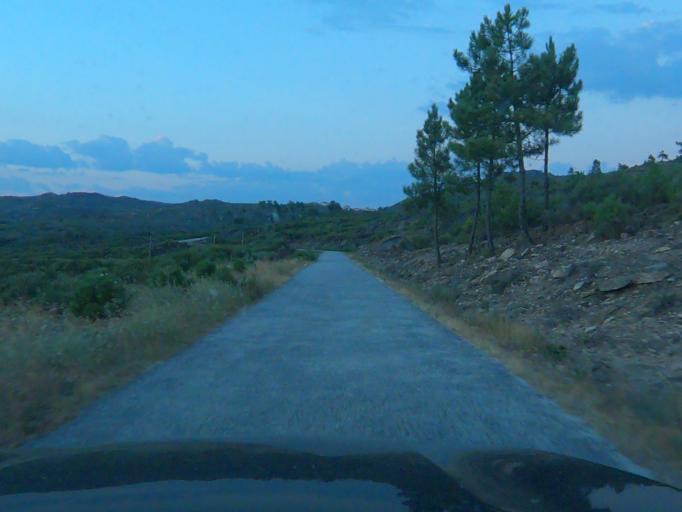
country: PT
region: Vila Real
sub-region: Sabrosa
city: Sabrosa
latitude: 41.2778
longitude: -7.6257
